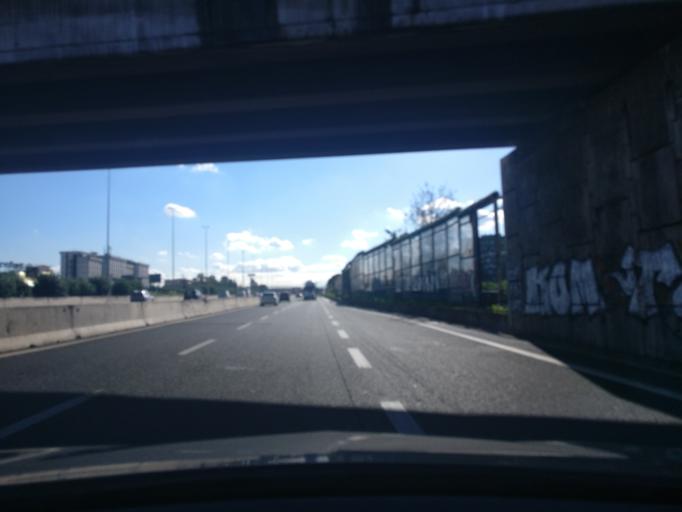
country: IT
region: Latium
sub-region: Citta metropolitana di Roma Capitale
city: Ciampino
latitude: 41.8532
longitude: 12.5971
